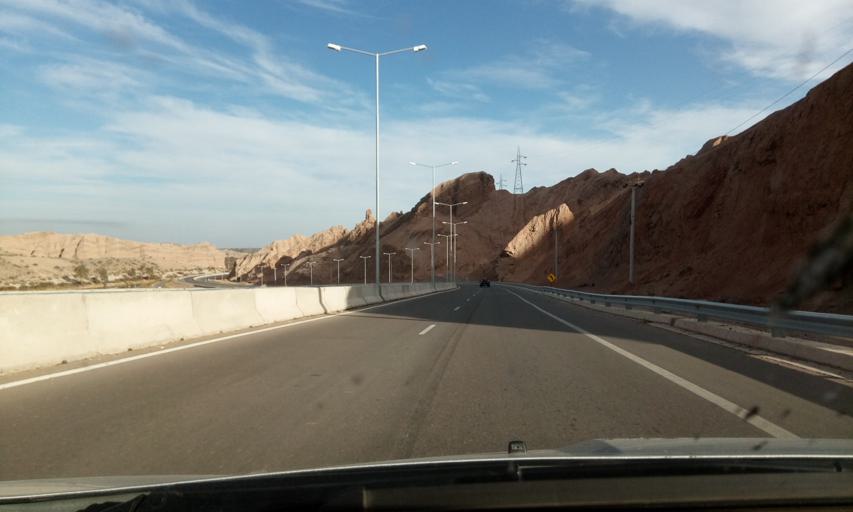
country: AR
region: San Juan
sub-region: Departamento de Rivadavia
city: Rivadavia
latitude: -31.4794
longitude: -68.6505
